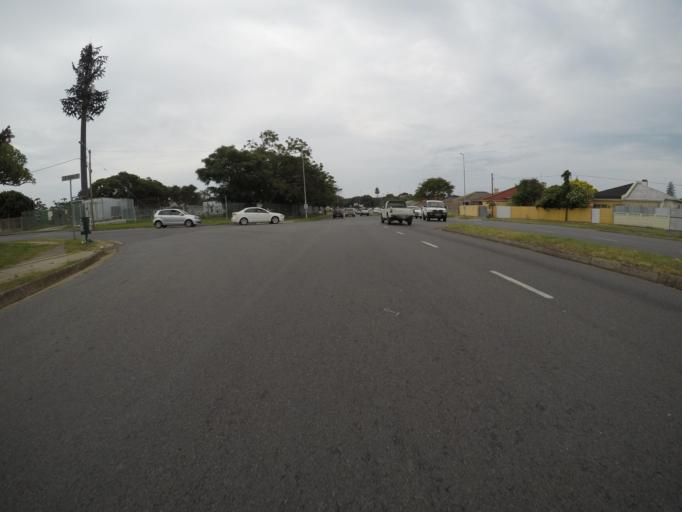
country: ZA
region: Eastern Cape
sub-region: Buffalo City Metropolitan Municipality
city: East London
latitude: -32.9963
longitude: 27.8940
